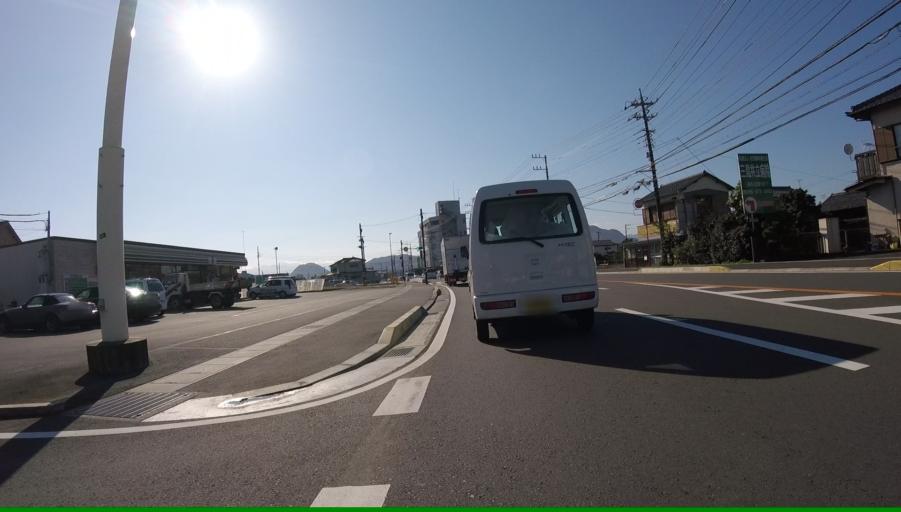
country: JP
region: Shizuoka
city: Mishima
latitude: 35.1006
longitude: 138.9152
